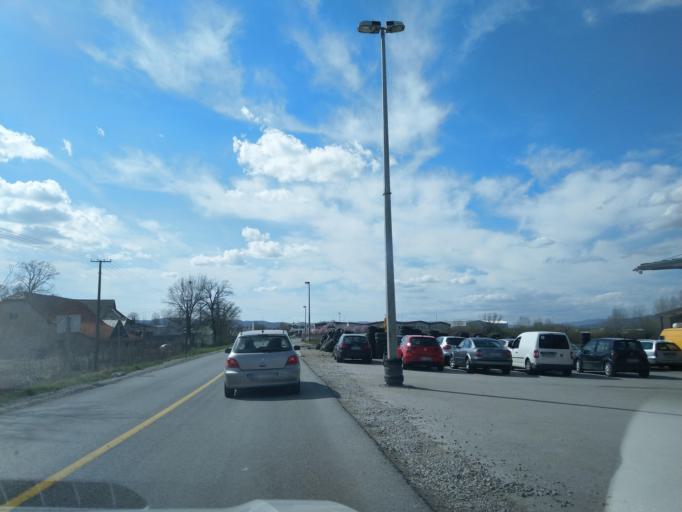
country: RS
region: Central Serbia
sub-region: Zlatiborski Okrug
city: Pozega
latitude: 43.8317
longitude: 20.0491
